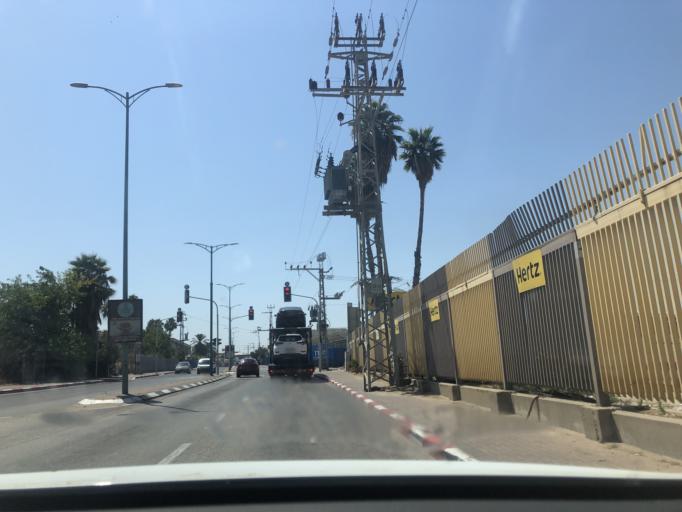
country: IL
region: Central District
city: Lod
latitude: 31.9687
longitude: 34.8965
